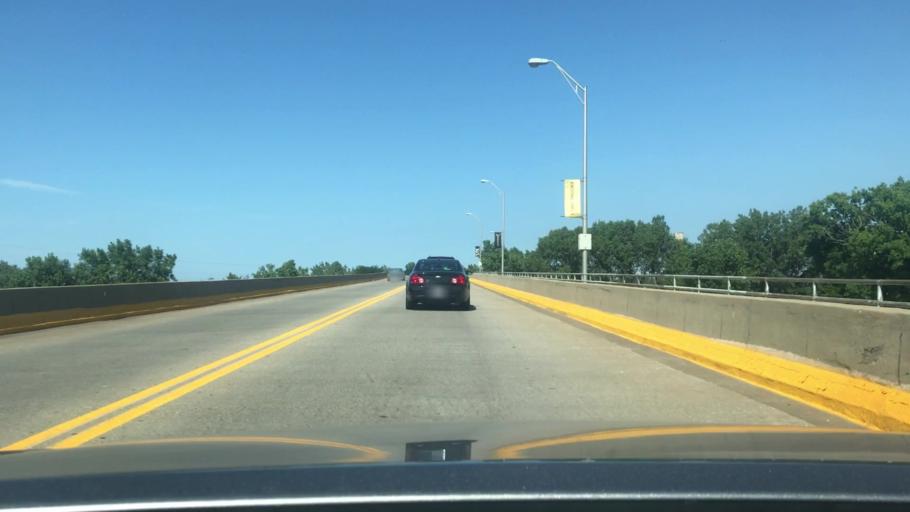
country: US
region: Indiana
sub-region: Lake County
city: Whiting
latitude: 41.6954
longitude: -87.5144
